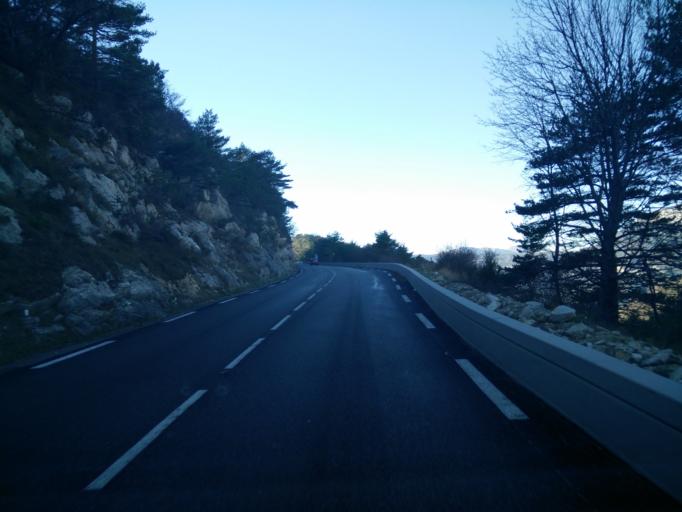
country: FR
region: Provence-Alpes-Cote d'Azur
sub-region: Departement des Alpes-Maritimes
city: Saint-Vallier-de-Thiey
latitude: 43.7115
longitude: 6.8419
